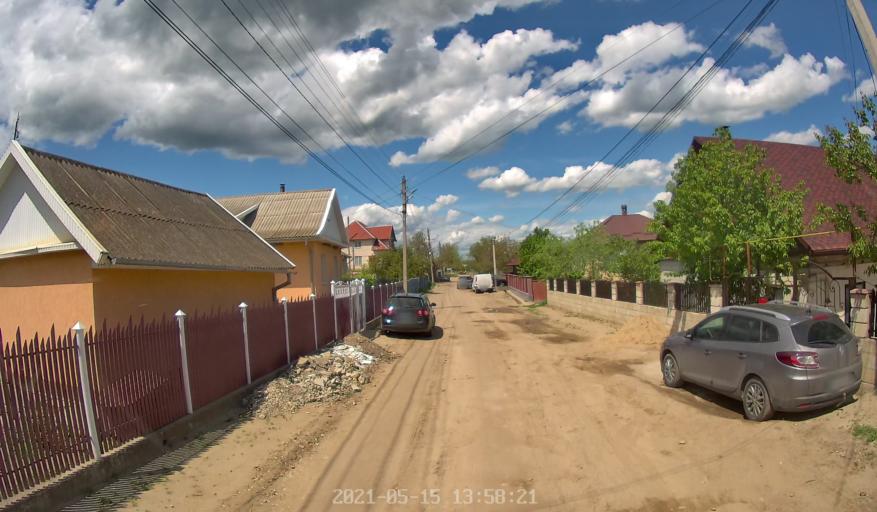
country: MD
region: Hincesti
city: Hincesti
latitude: 46.7415
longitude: 28.5133
